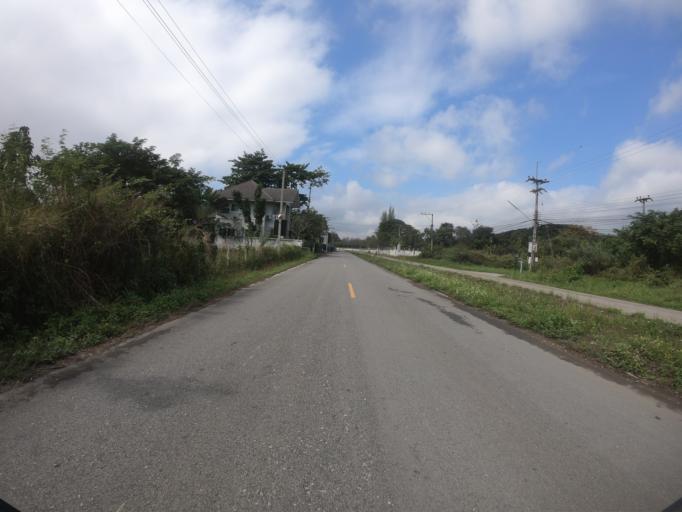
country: TH
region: Chiang Mai
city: Hang Dong
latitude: 18.7275
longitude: 98.9528
